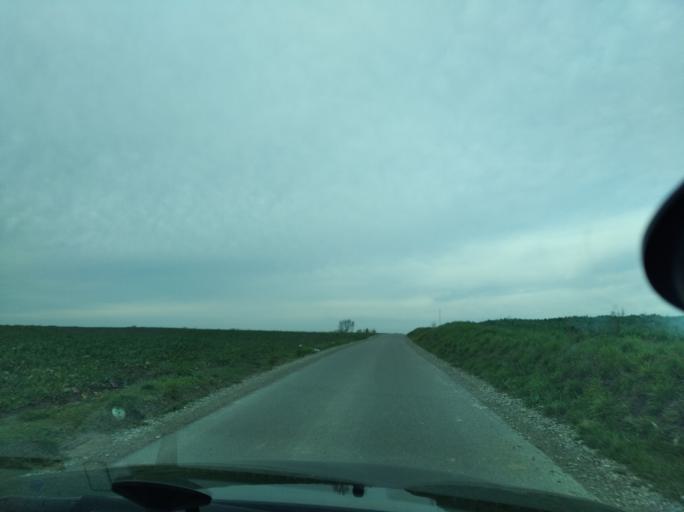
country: PL
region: Subcarpathian Voivodeship
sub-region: Powiat przeworski
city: Grzeska
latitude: 50.0679
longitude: 22.4624
